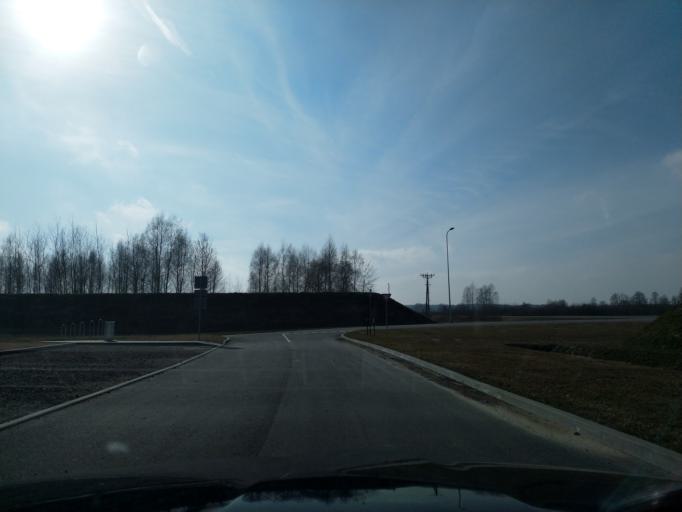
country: LV
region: Kuldigas Rajons
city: Kuldiga
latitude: 56.9554
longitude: 21.9822
